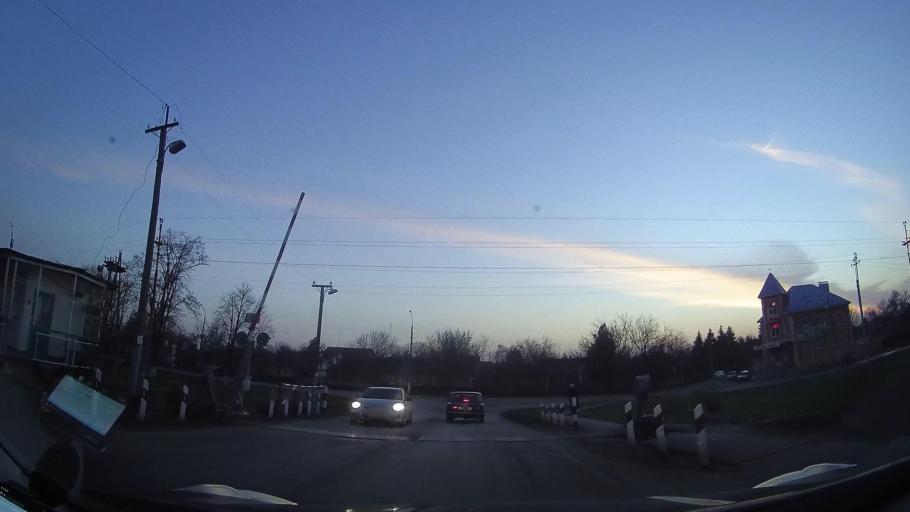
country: RU
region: Rostov
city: Zernograd
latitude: 46.8453
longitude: 40.2968
